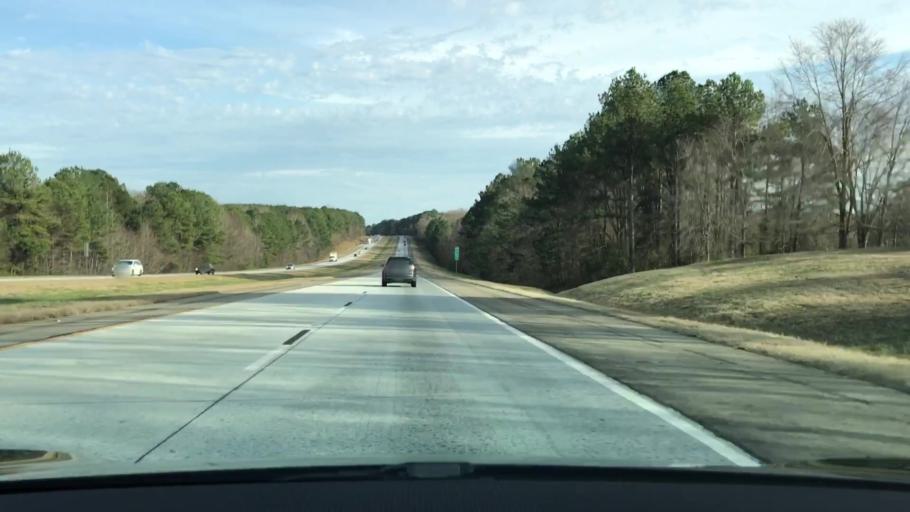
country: US
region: Georgia
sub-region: Putnam County
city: Jefferson
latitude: 33.5365
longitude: -83.3045
